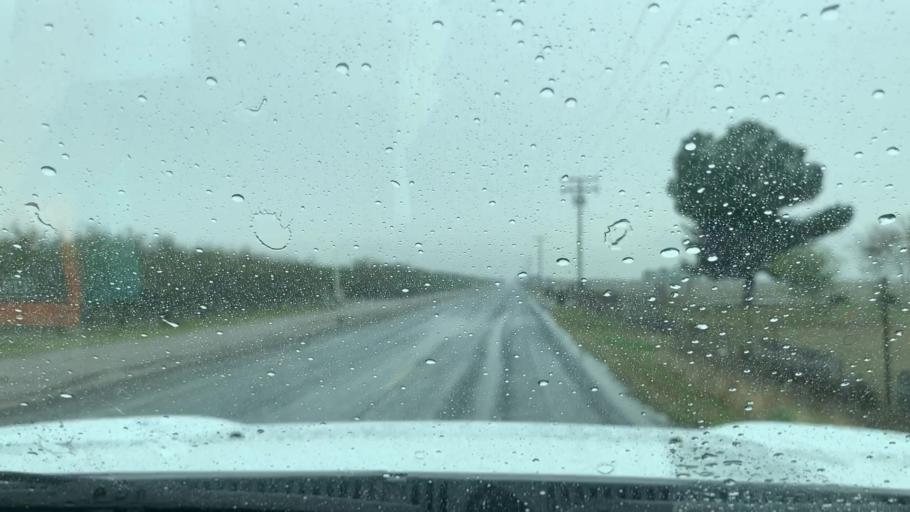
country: US
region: California
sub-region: Tulare County
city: Earlimart
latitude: 35.8919
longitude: -119.3303
